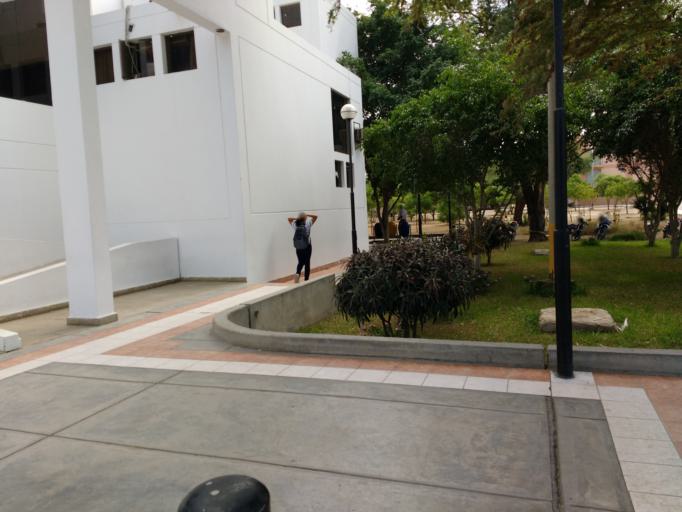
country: PE
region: Piura
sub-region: Provincia de Piura
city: Piura
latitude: -5.1825
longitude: -80.6191
